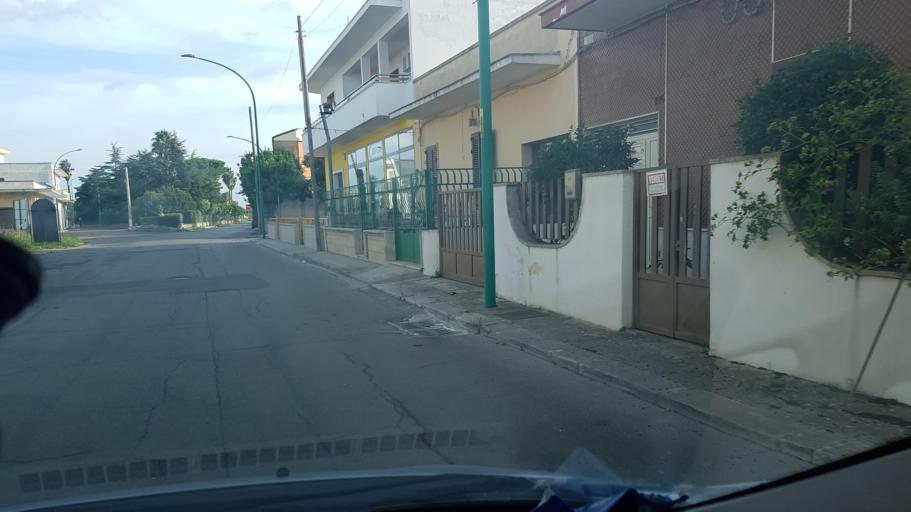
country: IT
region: Apulia
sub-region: Provincia di Lecce
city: Veglie
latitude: 40.3307
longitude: 17.9730
